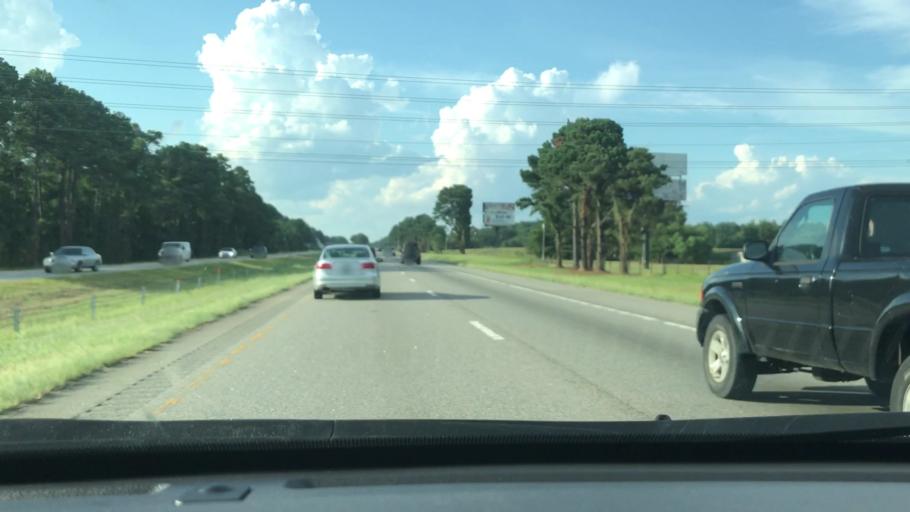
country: US
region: North Carolina
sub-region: Robeson County
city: Lumberton
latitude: 34.6942
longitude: -78.9984
